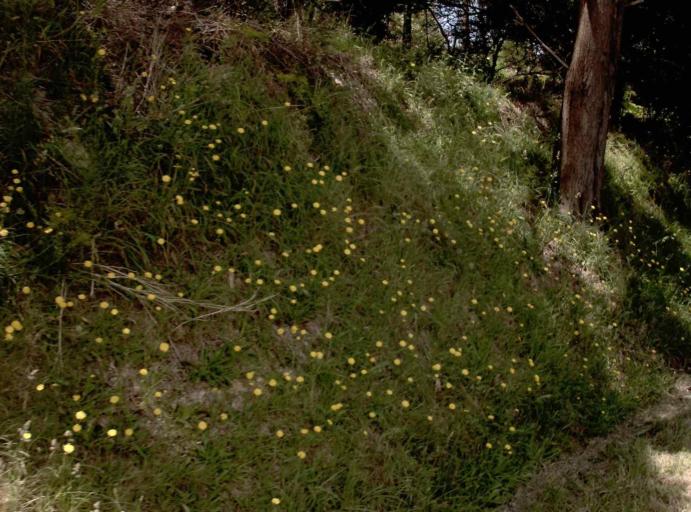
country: AU
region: Victoria
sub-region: Bass Coast
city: North Wonthaggi
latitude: -38.7239
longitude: 146.1210
